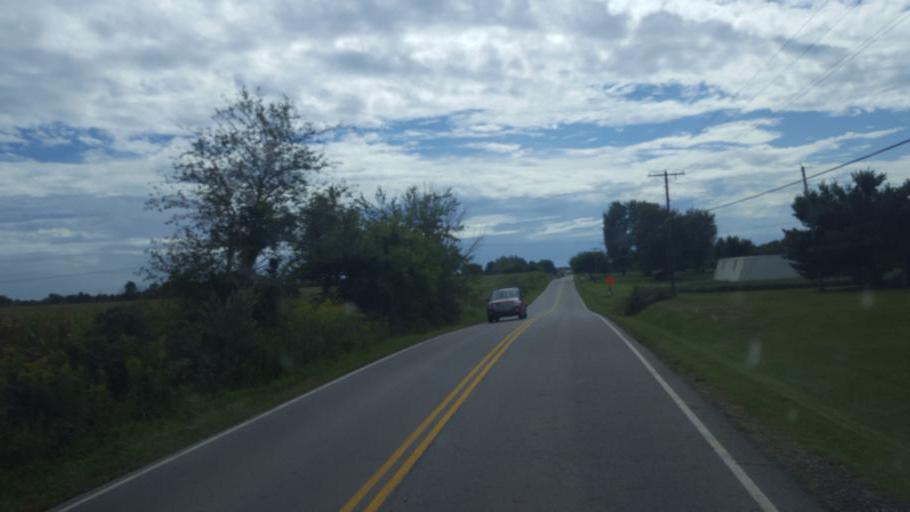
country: US
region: Ohio
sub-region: Licking County
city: Johnstown
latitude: 40.0902
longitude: -82.7156
